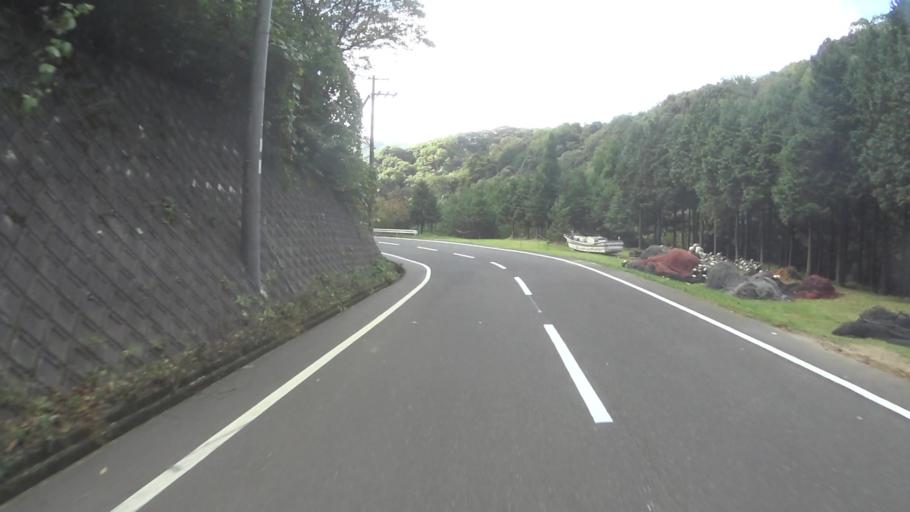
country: JP
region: Kyoto
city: Maizuru
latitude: 35.5610
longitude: 135.4300
